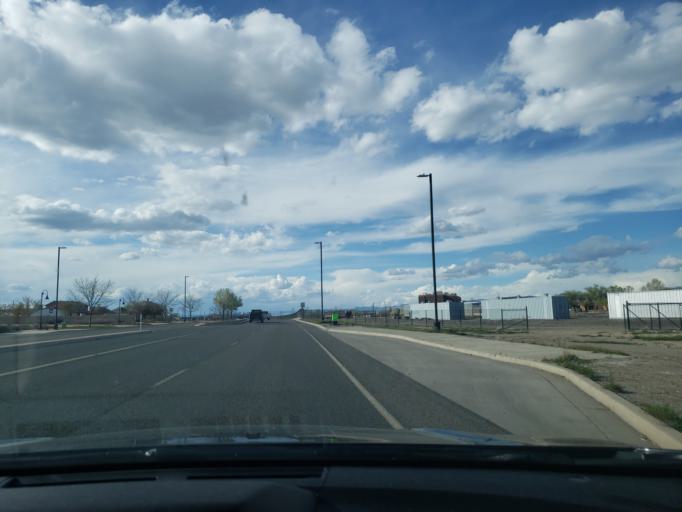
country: US
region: Colorado
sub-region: Mesa County
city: Grand Junction
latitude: 39.0628
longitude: -108.5719
